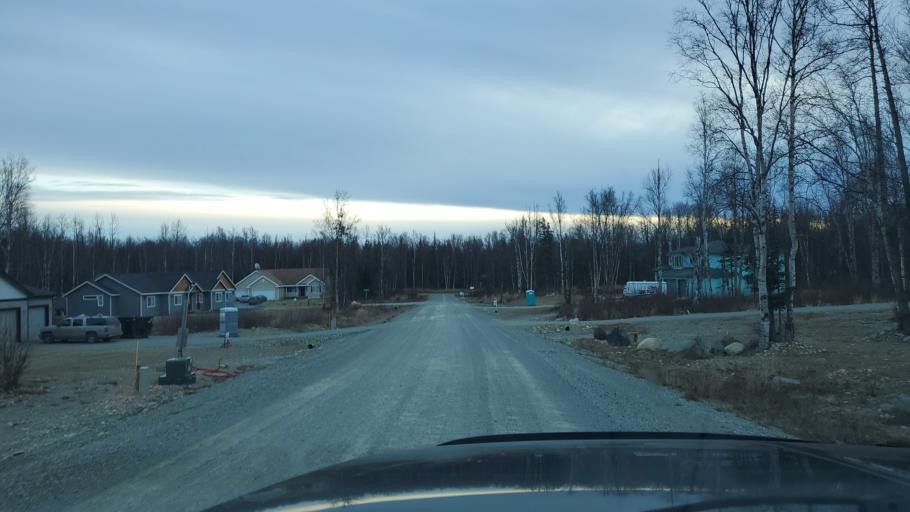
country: US
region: Alaska
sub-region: Matanuska-Susitna Borough
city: Lakes
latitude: 61.6555
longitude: -149.2910
